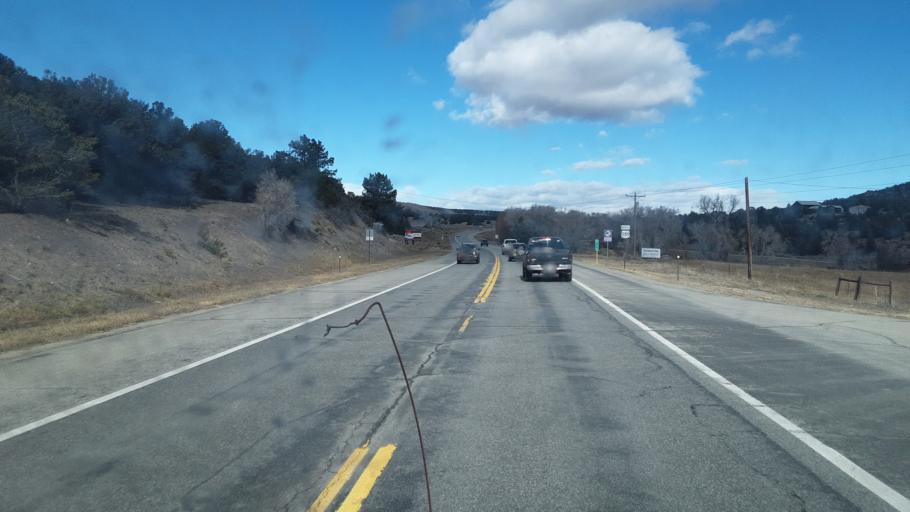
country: US
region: Colorado
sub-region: Chaffee County
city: Salida
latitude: 38.6336
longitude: -106.0797
